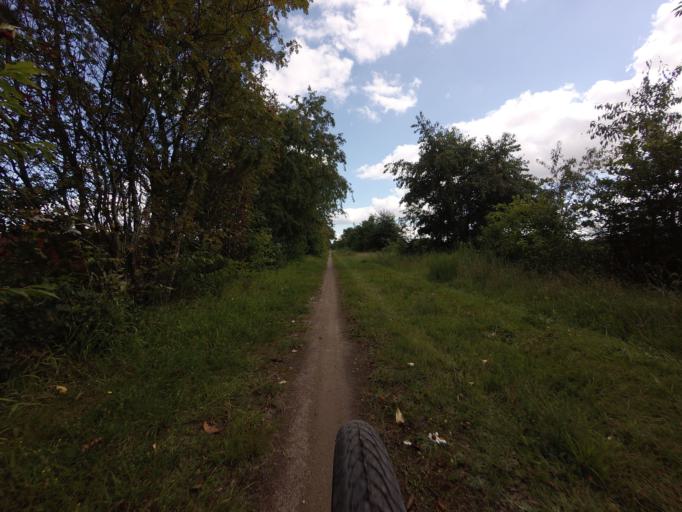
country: DK
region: Central Jutland
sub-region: Ikast-Brande Kommune
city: Brande
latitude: 55.9782
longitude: 9.2481
